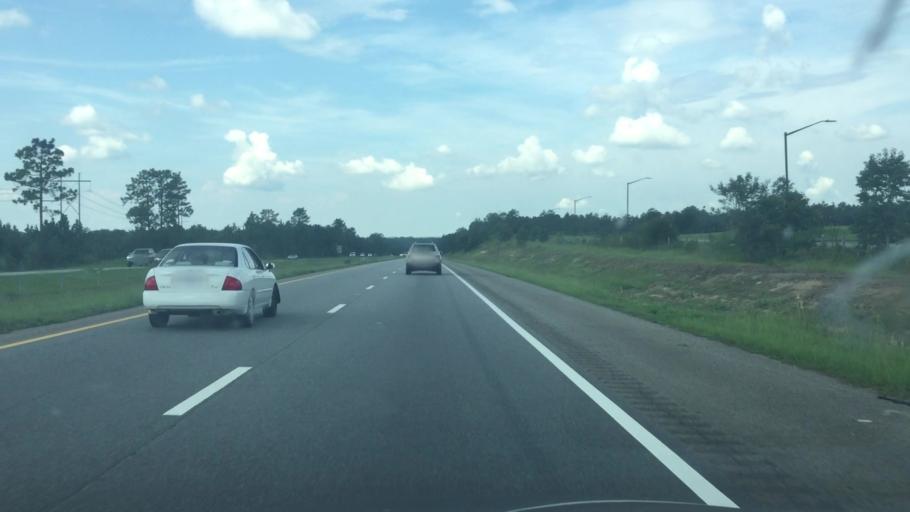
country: US
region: North Carolina
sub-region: Richmond County
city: Hamlet
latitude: 34.8542
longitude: -79.7128
